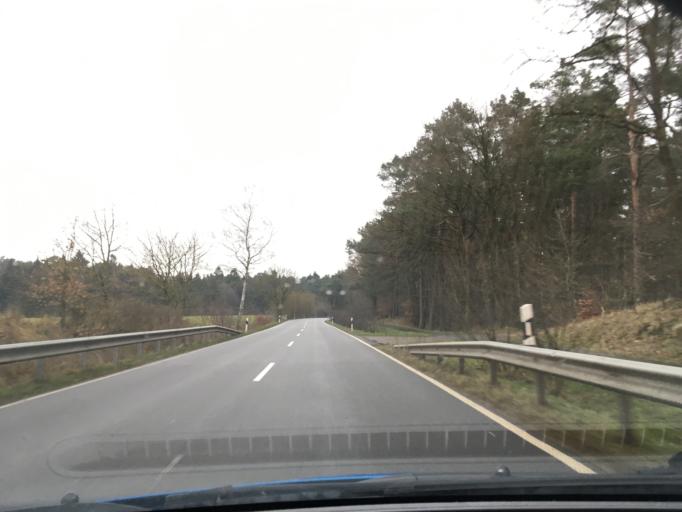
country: DE
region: Schleswig-Holstein
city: Roseburg
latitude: 53.5391
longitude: 10.6356
